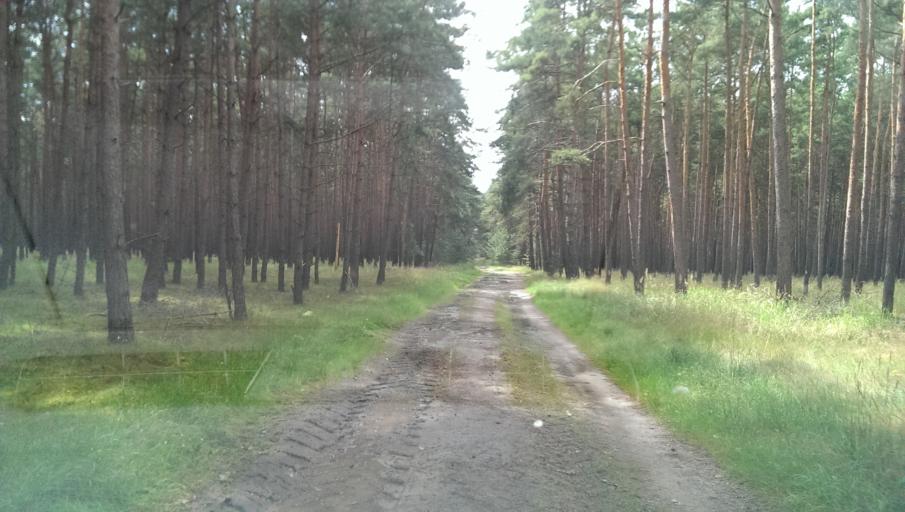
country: DE
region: Brandenburg
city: Linthe
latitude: 52.1519
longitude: 12.7600
